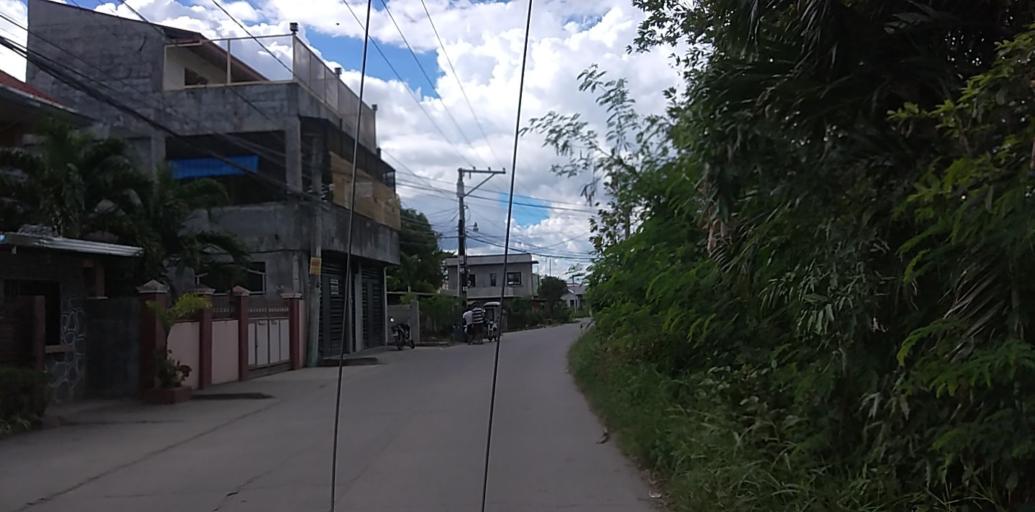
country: PH
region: Central Luzon
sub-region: Province of Pampanga
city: Arayat
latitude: 15.1396
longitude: 120.7750
